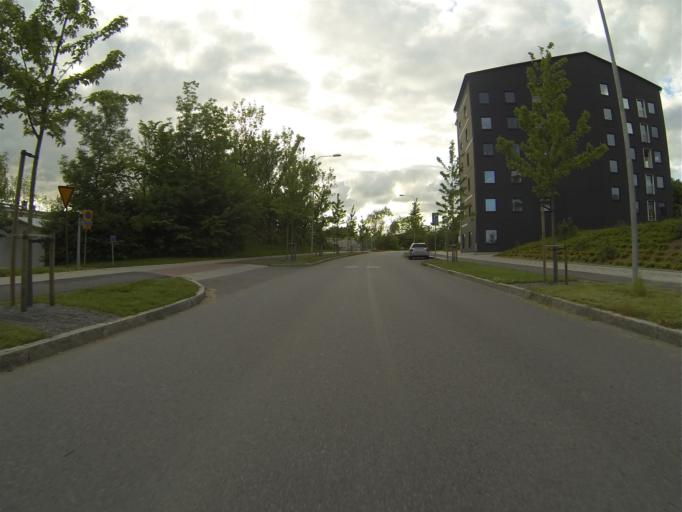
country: SE
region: Skane
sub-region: Lunds Kommun
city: Lund
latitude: 55.6957
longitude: 13.2358
